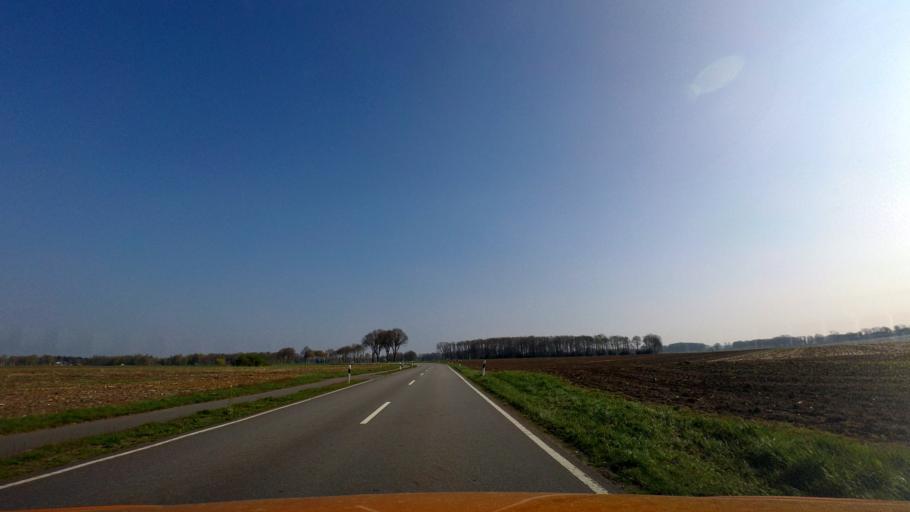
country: DE
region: Lower Saxony
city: Dinklage
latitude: 52.7033
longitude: 8.1558
